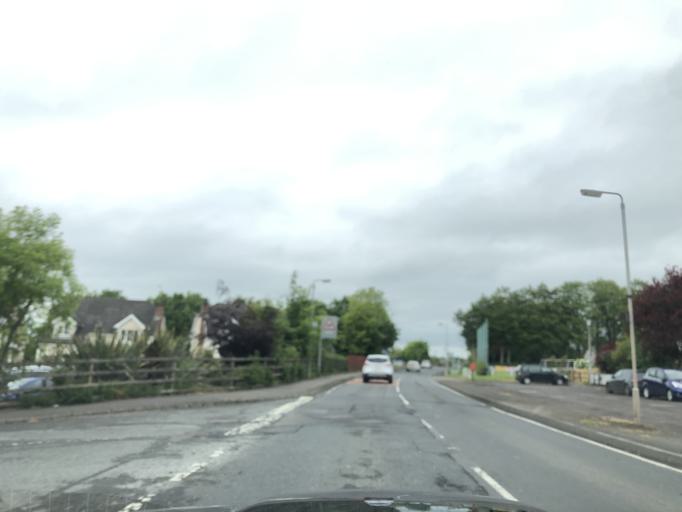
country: GB
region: Northern Ireland
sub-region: Antrim Borough
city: Templepatrick
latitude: 54.6125
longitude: -6.1211
